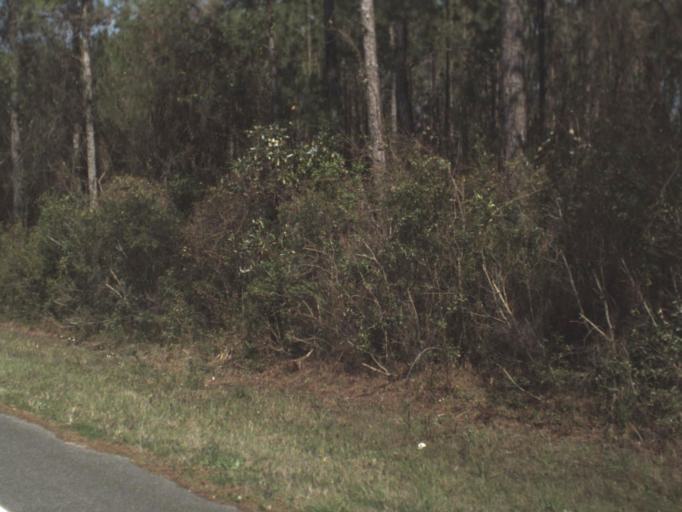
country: US
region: Florida
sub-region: Franklin County
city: Carrabelle
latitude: 29.9663
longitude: -84.5002
